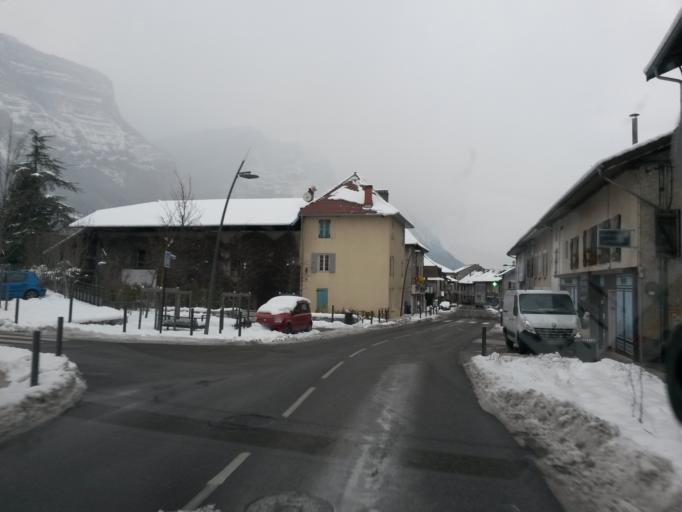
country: FR
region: Rhone-Alpes
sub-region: Departement de l'Isere
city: Bernin
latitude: 45.2711
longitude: 5.8680
